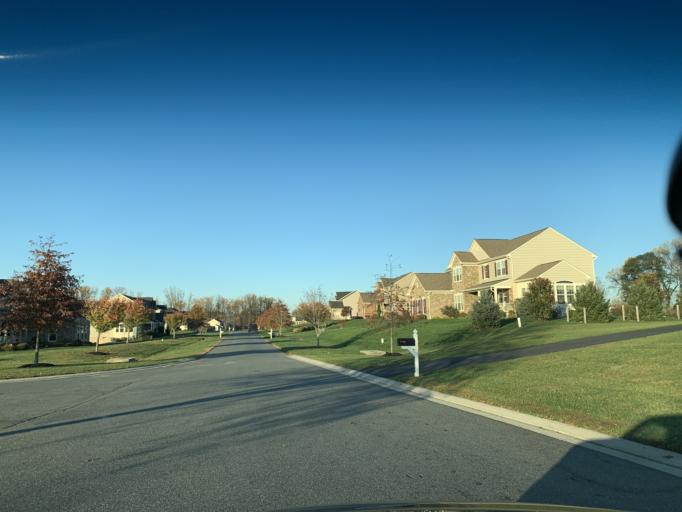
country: US
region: Maryland
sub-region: Harford County
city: Bel Air North
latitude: 39.5466
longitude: -76.4037
